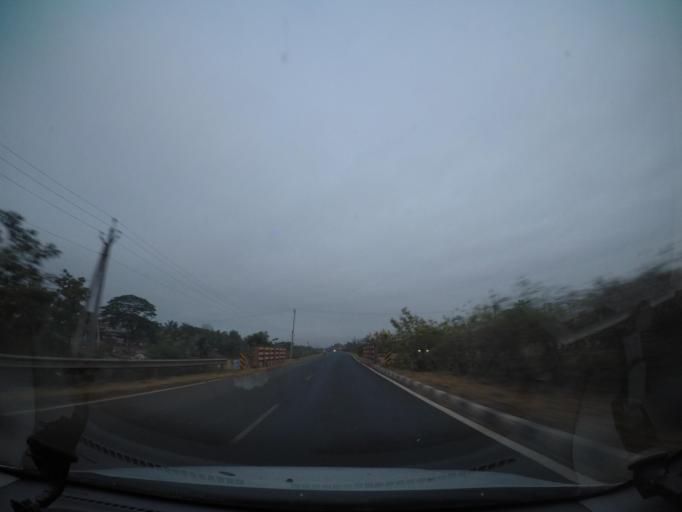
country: IN
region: Andhra Pradesh
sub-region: West Godavari
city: Tadepallegudem
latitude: 16.8088
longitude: 81.3206
